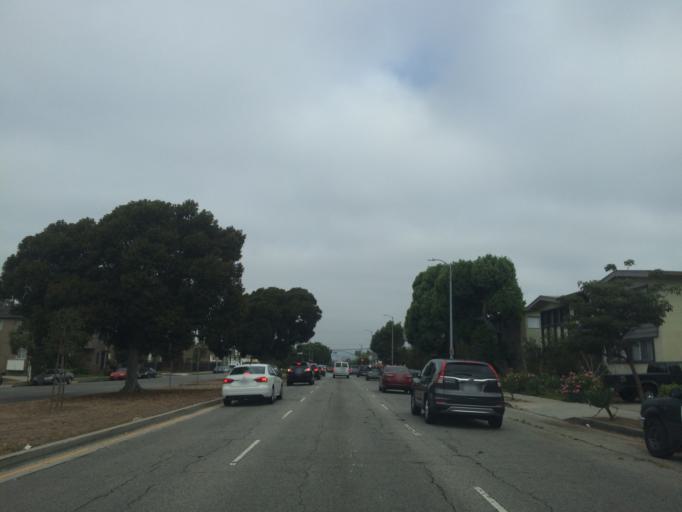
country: US
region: California
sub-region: Los Angeles County
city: West Hollywood
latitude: 34.0534
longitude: -118.3527
